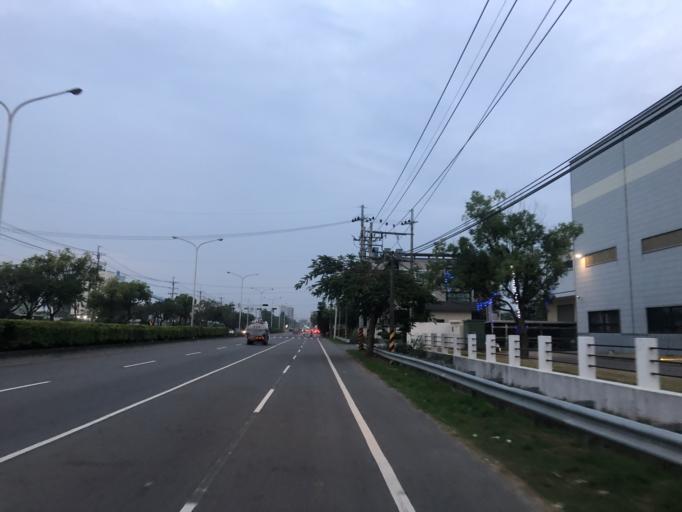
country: TW
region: Taiwan
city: Yujing
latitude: 23.1129
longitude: 120.3185
